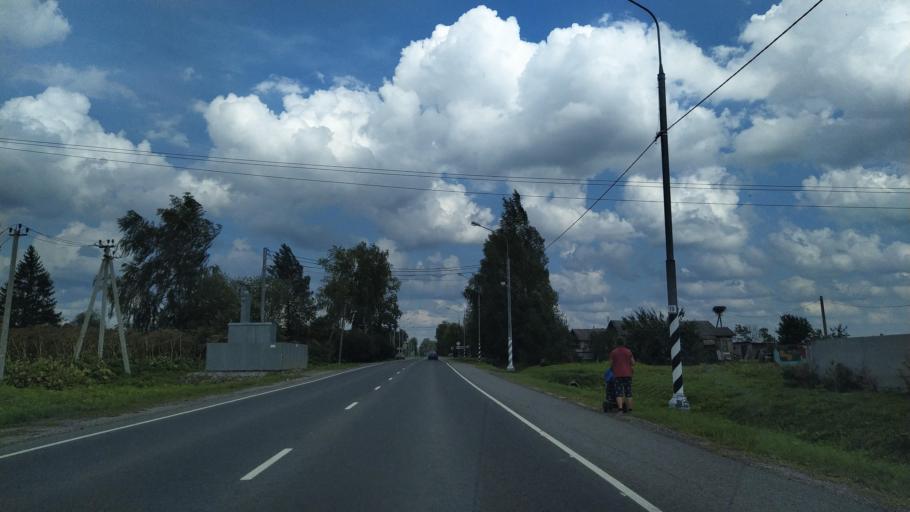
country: RU
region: Novgorod
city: Sol'tsy
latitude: 58.0817
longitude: 30.0948
